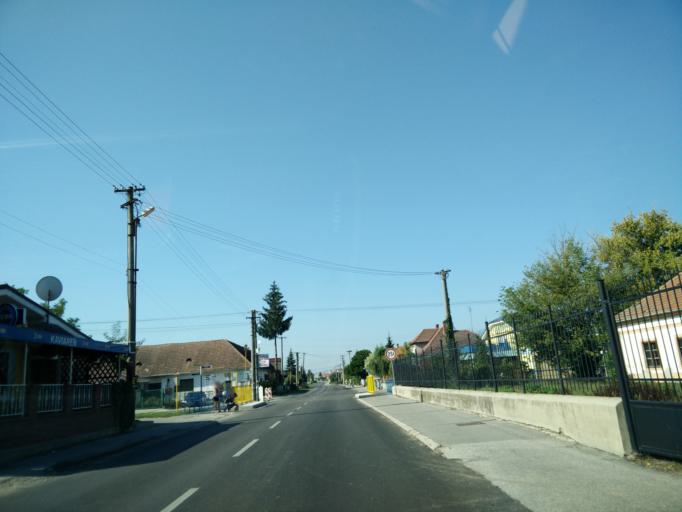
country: SK
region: Nitriansky
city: Banovce nad Bebravou
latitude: 48.5362
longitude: 18.1984
